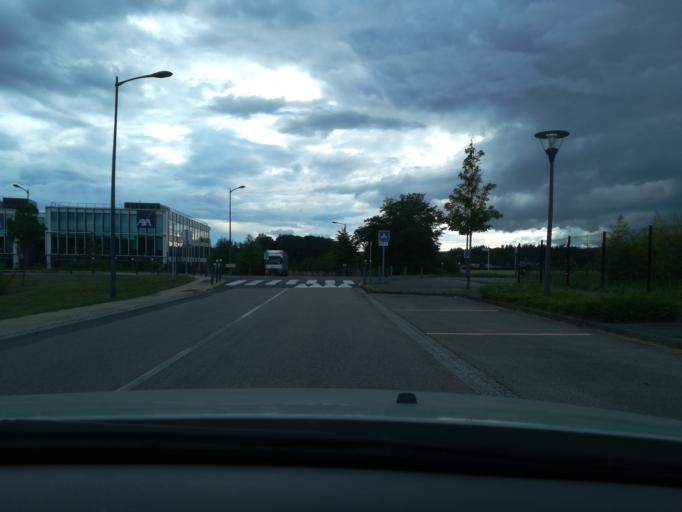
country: FR
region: Haute-Normandie
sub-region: Departement de la Seine-Maritime
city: Isneauville
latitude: 49.4910
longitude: 1.1395
